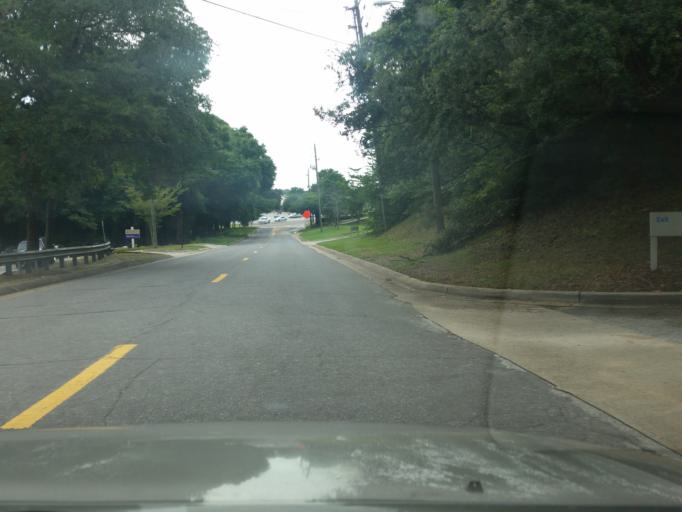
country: US
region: Florida
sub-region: Escambia County
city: Brent
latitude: 30.4713
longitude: -87.2109
